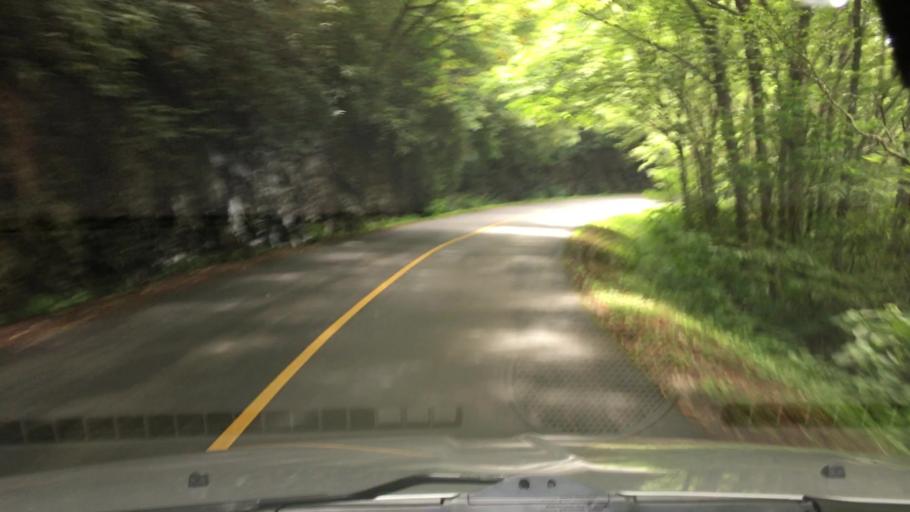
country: US
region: North Carolina
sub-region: Buncombe County
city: Swannanoa
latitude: 35.7008
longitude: -82.3961
